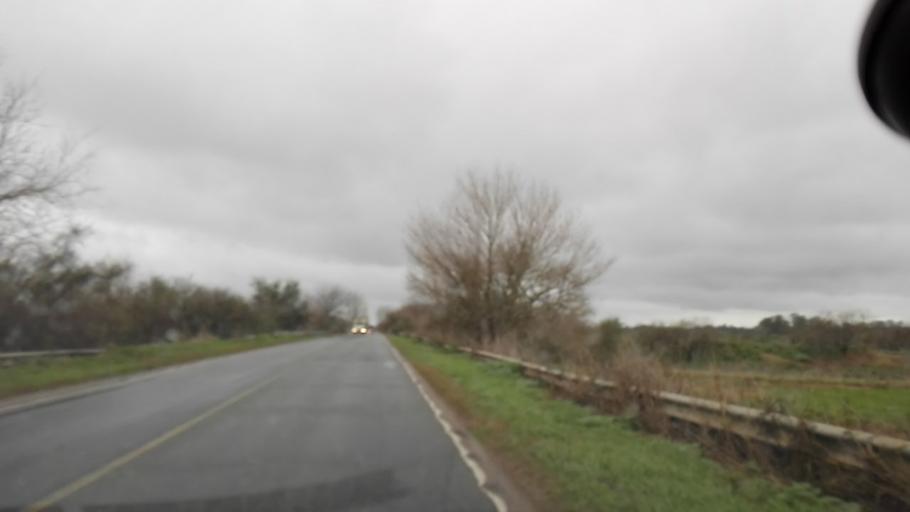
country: AR
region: Buenos Aires
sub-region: Partido de Brandsen
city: Brandsen
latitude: -35.1800
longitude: -58.2581
